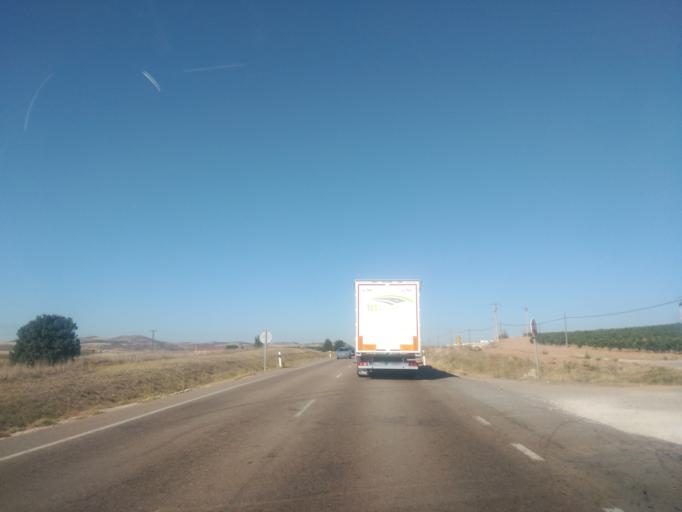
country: ES
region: Castille and Leon
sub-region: Provincia de Valladolid
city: Manzanillo
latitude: 41.6091
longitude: -4.1553
